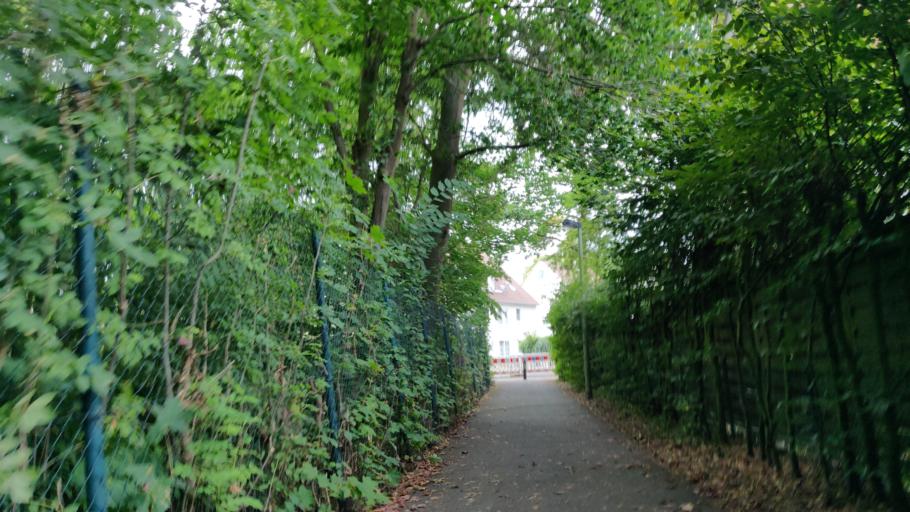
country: DE
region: Lower Saxony
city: Lilienthal
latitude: 53.0965
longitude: 8.8753
